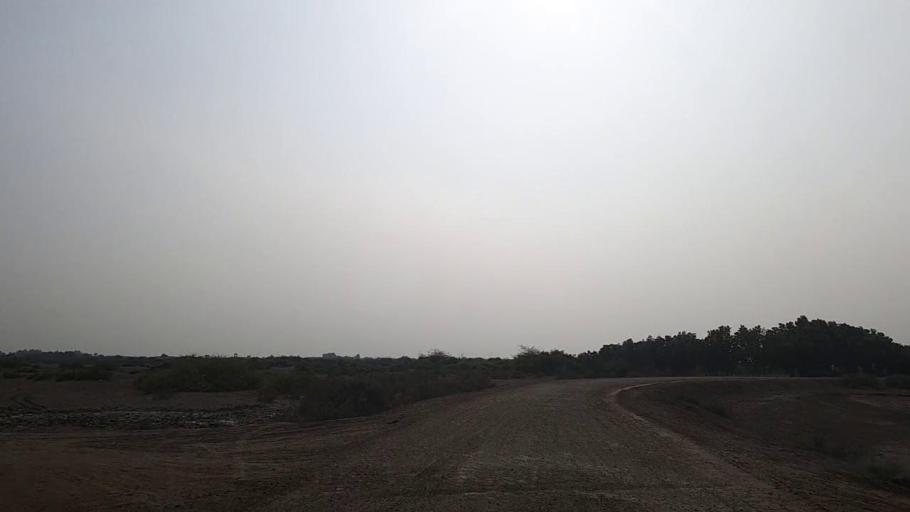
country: PK
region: Sindh
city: Mirpur Sakro
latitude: 24.6449
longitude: 67.6149
